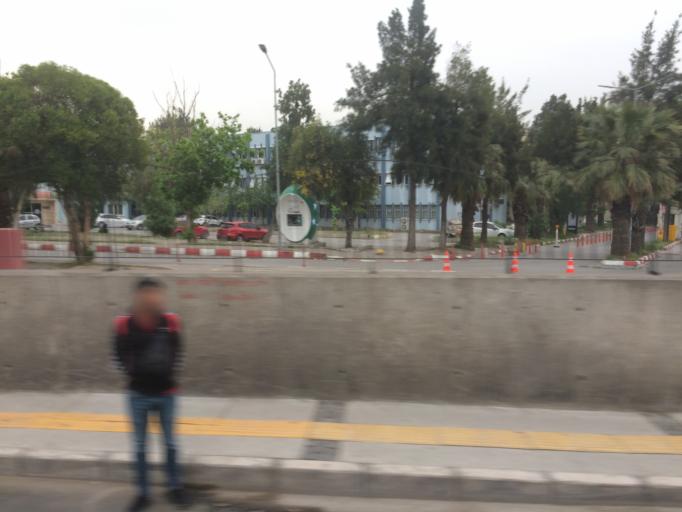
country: TR
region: Izmir
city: Bornova
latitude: 38.4569
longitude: 27.2080
